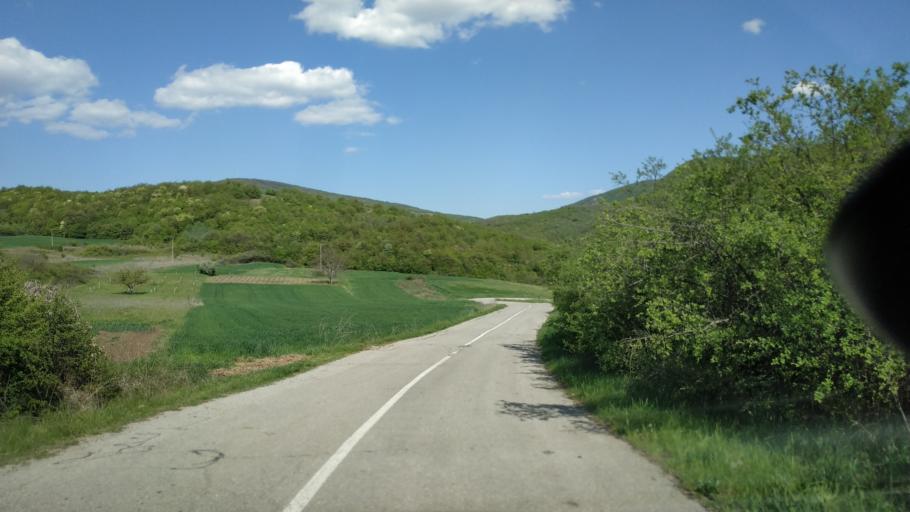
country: RS
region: Central Serbia
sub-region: Nisavski Okrug
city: Nis
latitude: 43.4291
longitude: 21.8494
